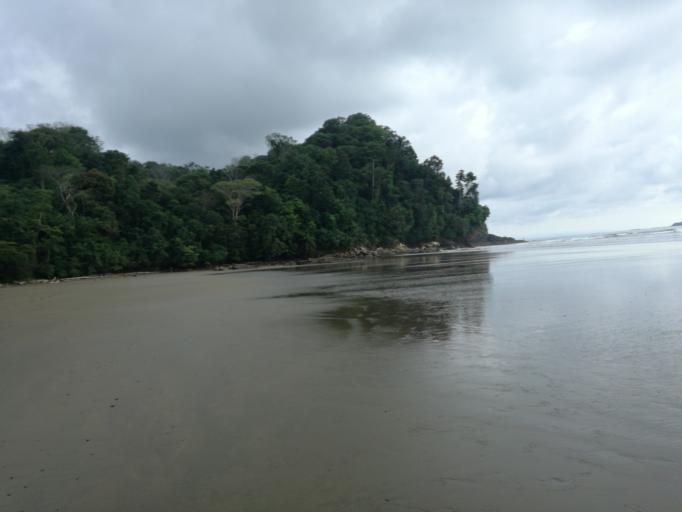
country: CR
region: San Jose
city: Mercedes
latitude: 9.1461
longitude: -83.7291
